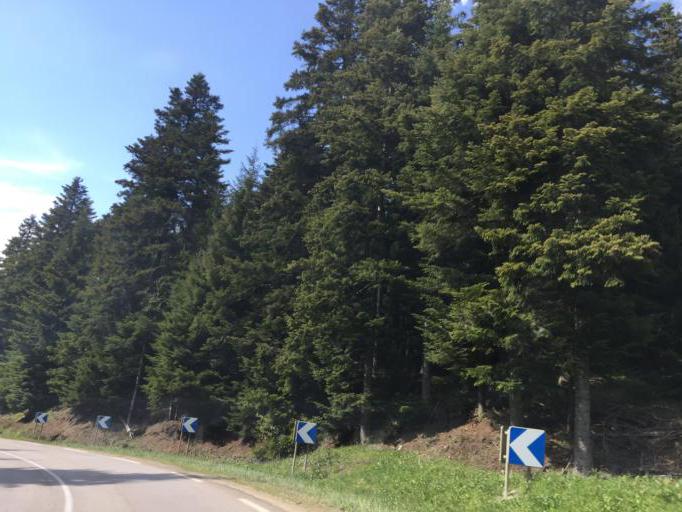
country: FR
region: Rhone-Alpes
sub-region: Departement de la Loire
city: Saint-Genest-Malifaux
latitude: 45.3451
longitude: 4.4834
